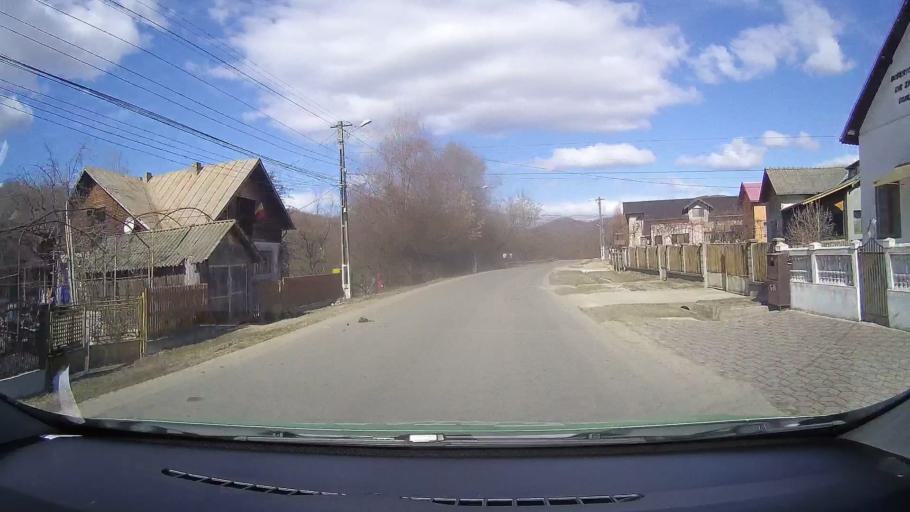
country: RO
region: Dambovita
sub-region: Comuna Vulcana-Pandele
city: Gura Vulcanei
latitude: 45.0367
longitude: 25.3913
